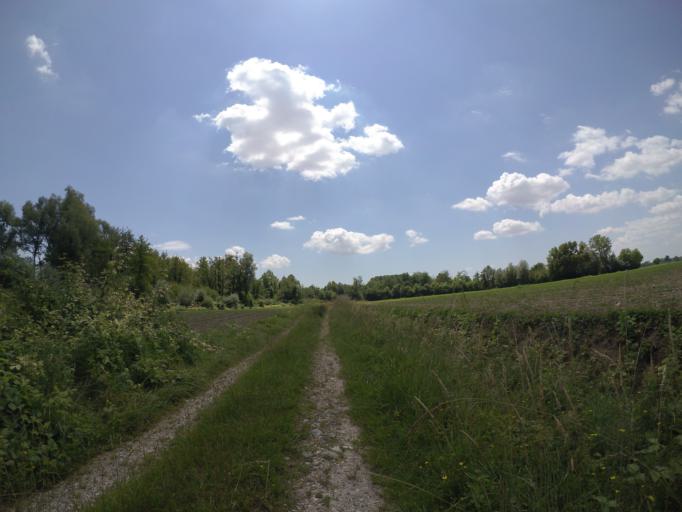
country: IT
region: Friuli Venezia Giulia
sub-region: Provincia di Udine
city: Bertiolo
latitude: 45.9330
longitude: 13.0752
